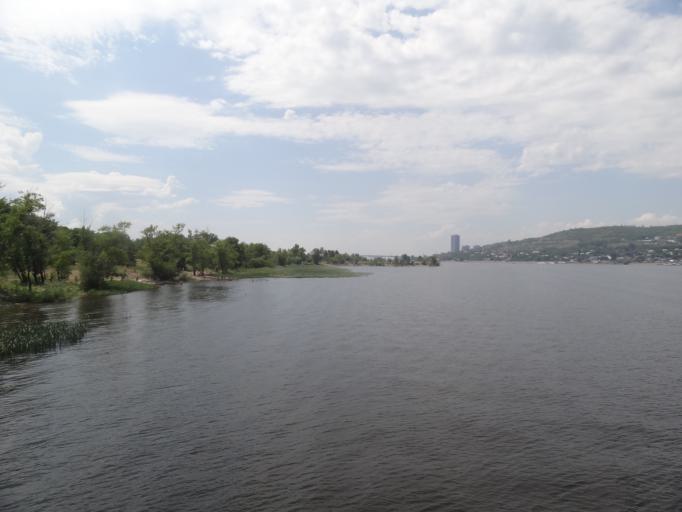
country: RU
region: Saratov
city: Engel's
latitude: 51.5443
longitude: 46.0960
